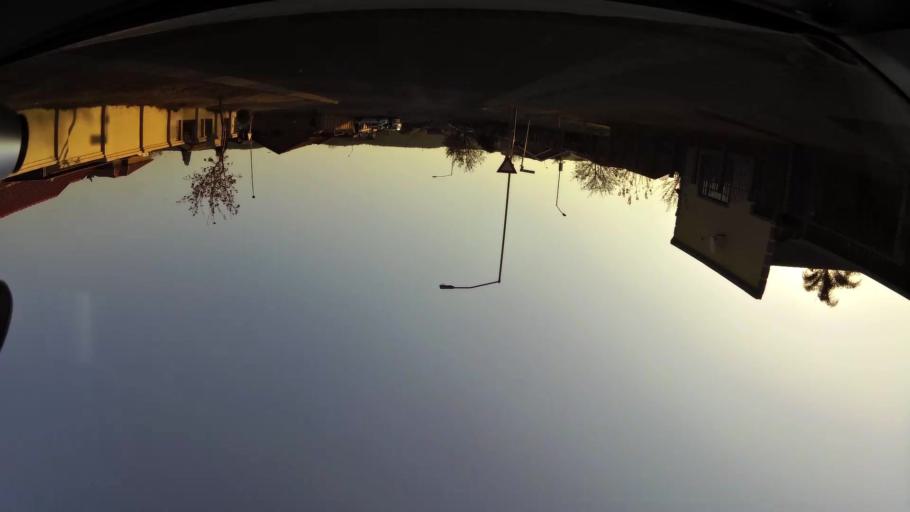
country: ZA
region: Gauteng
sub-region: City of Tshwane Metropolitan Municipality
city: Pretoria
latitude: -25.7463
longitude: 28.1170
